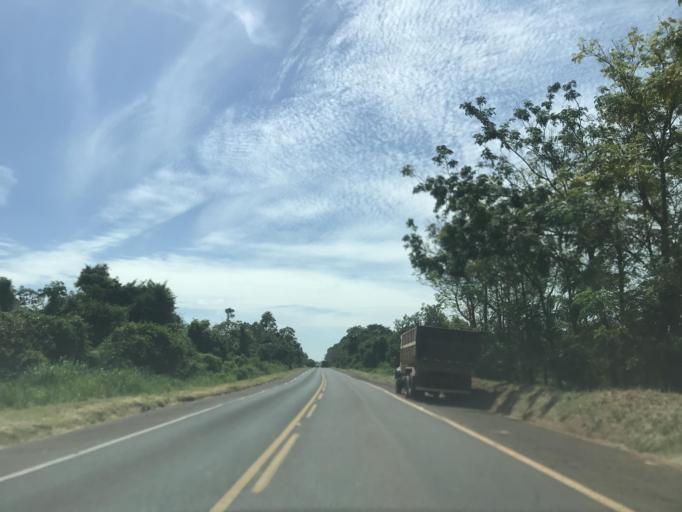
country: BR
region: Parana
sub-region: Paranavai
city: Nova Aurora
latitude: -22.9595
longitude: -52.6834
